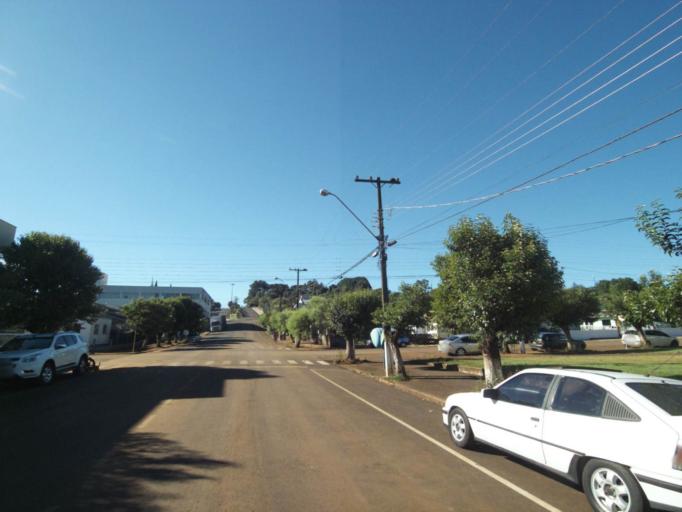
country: BR
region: Santa Catarina
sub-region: Sao Lourenco Do Oeste
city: Sao Lourenco dOeste
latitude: -26.2651
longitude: -52.7831
